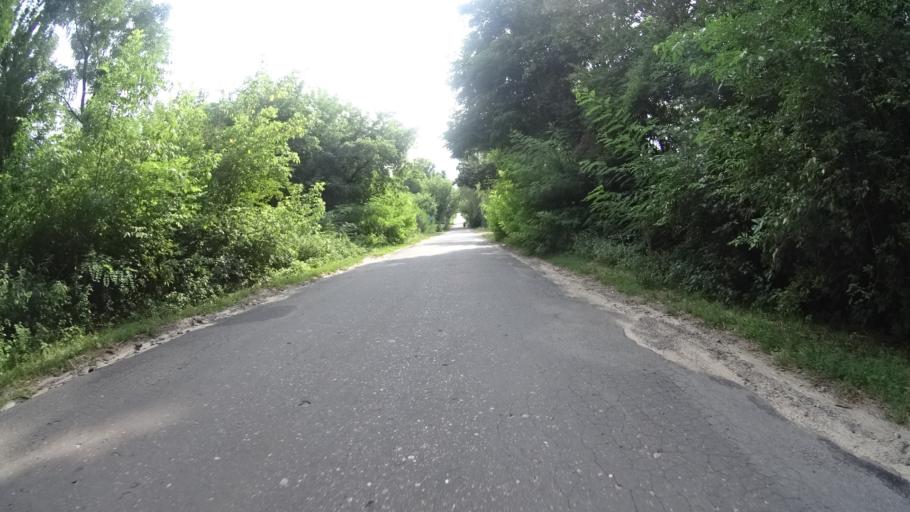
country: PL
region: Masovian Voivodeship
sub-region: Powiat bialobrzeski
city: Wysmierzyce
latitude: 51.6573
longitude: 20.7768
